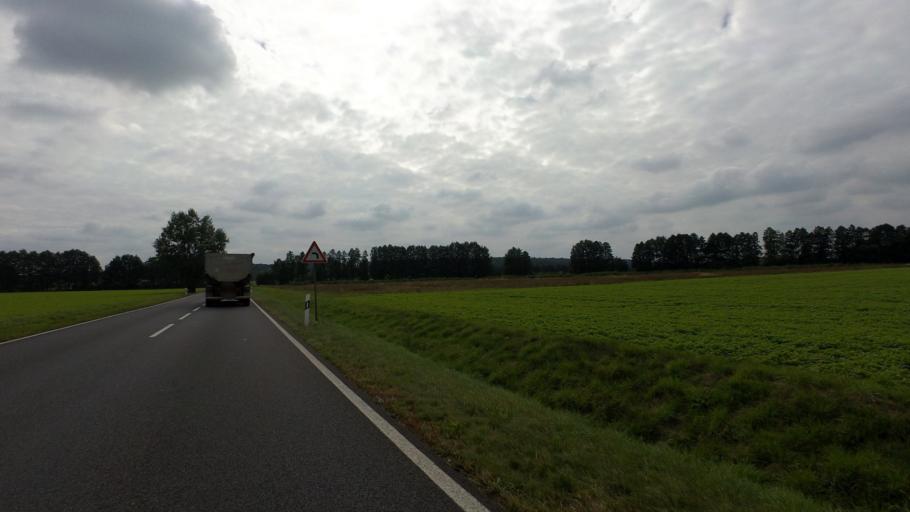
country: DE
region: Brandenburg
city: Kasel-Golzig
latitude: 51.9062
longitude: 13.6733
